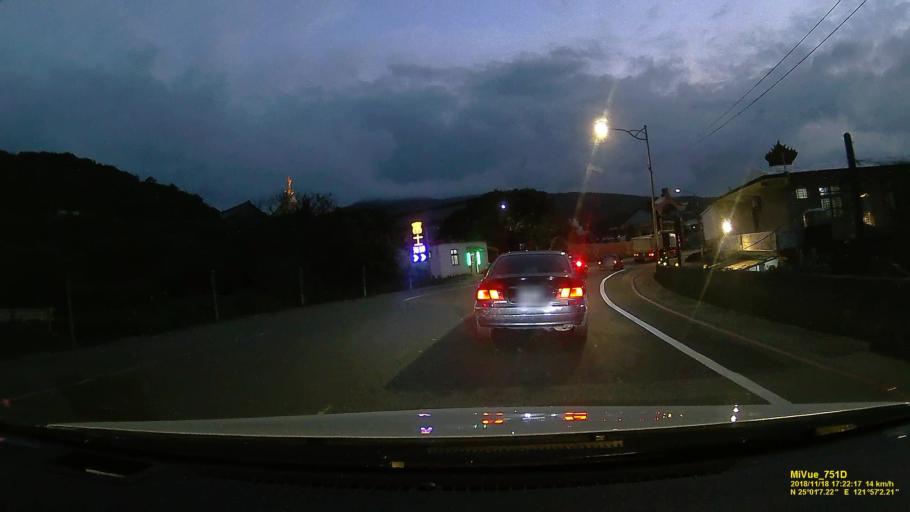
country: TW
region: Taiwan
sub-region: Keelung
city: Keelung
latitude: 25.0186
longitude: 121.9506
